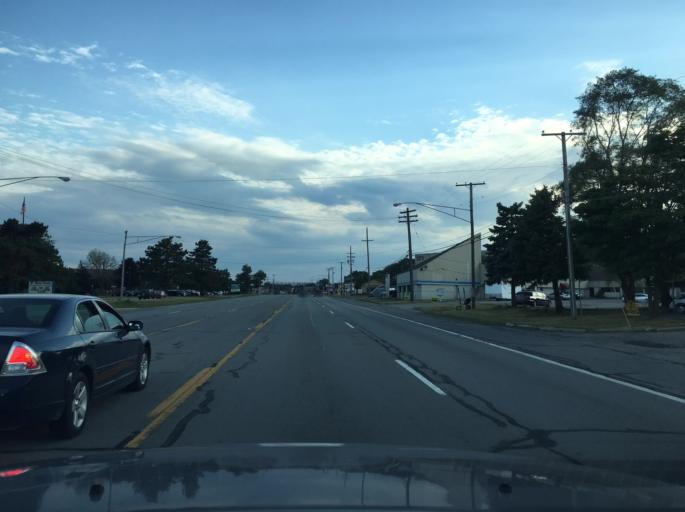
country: US
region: Michigan
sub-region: Macomb County
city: Mount Clemens
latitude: 42.6111
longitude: -82.8924
